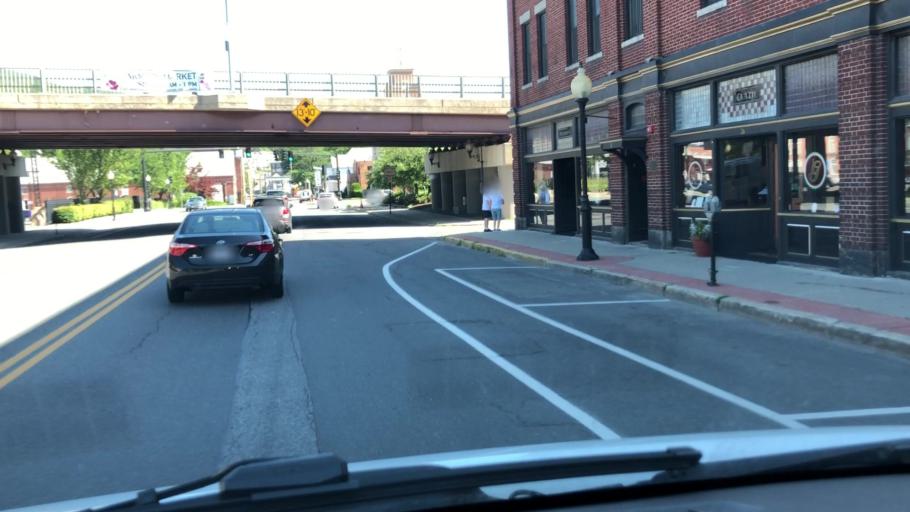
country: US
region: Massachusetts
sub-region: Berkshire County
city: North Adams
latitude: 42.7000
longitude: -73.1136
